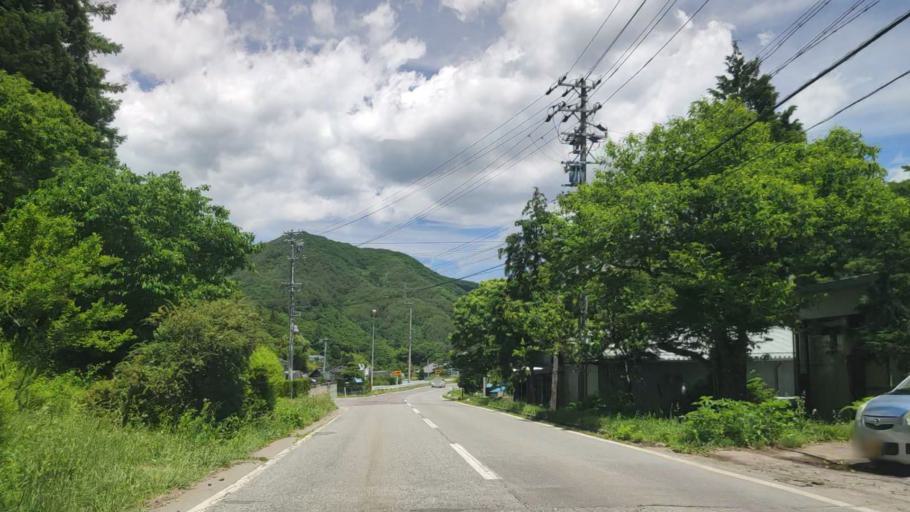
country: JP
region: Nagano
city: Kamimaruko
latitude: 36.1971
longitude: 138.2428
